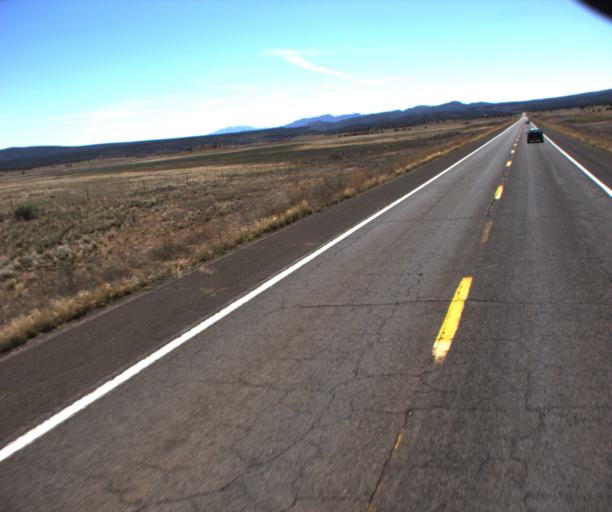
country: US
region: Arizona
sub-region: Mohave County
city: Peach Springs
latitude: 35.4714
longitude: -113.5912
